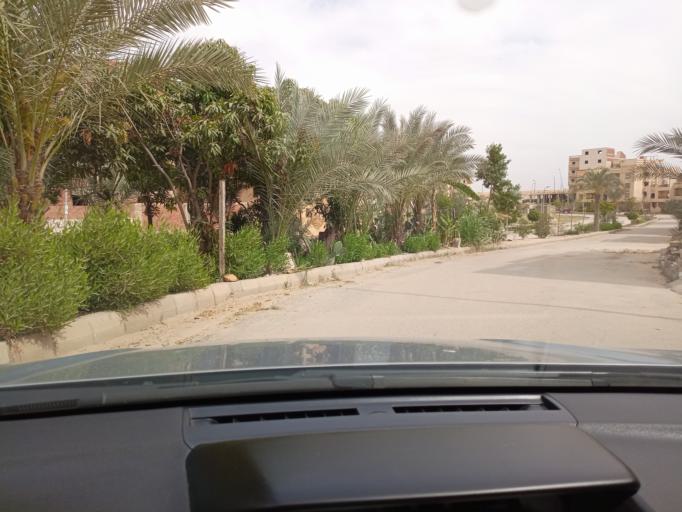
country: EG
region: Muhafazat al Qalyubiyah
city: Al Khankah
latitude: 30.2452
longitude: 31.4899
